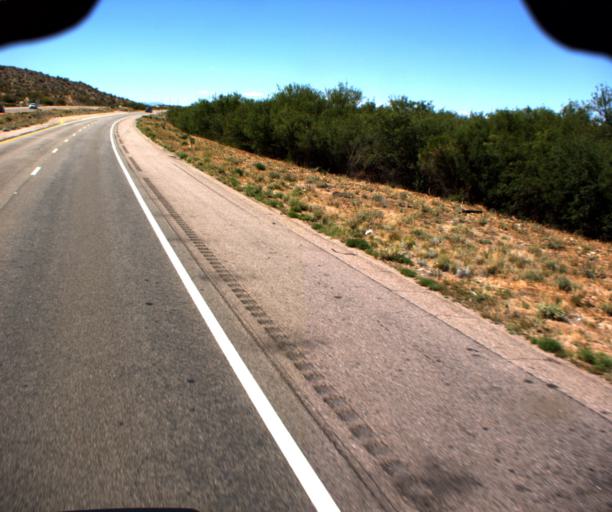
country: US
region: Arizona
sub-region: Yavapai County
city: Bagdad
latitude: 34.6676
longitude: -113.5857
